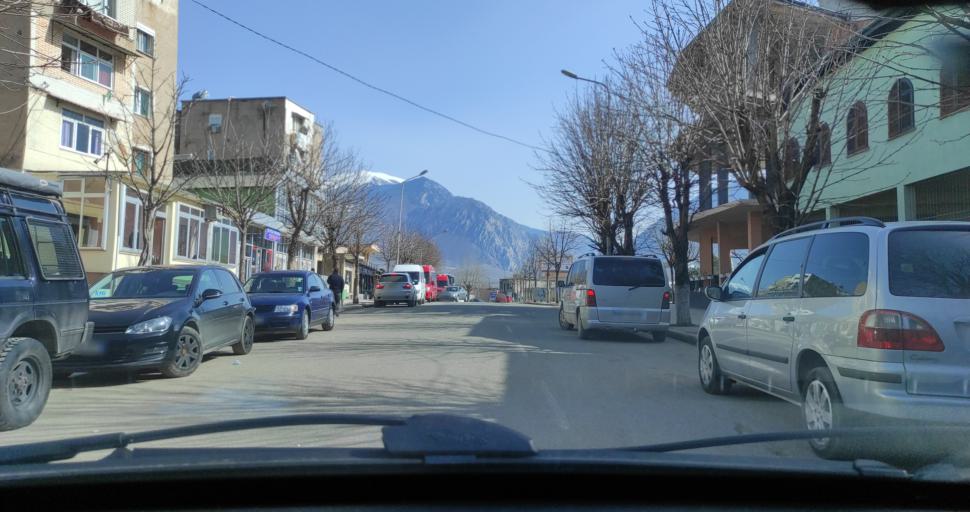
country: AL
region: Kukes
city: Kukes
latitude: 42.0756
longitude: 20.4243
